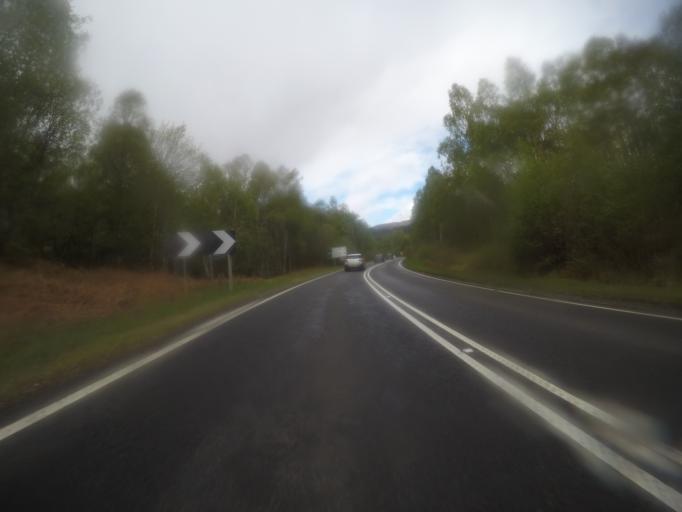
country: GB
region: Scotland
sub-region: Highland
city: Spean Bridge
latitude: 57.0823
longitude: -4.8981
